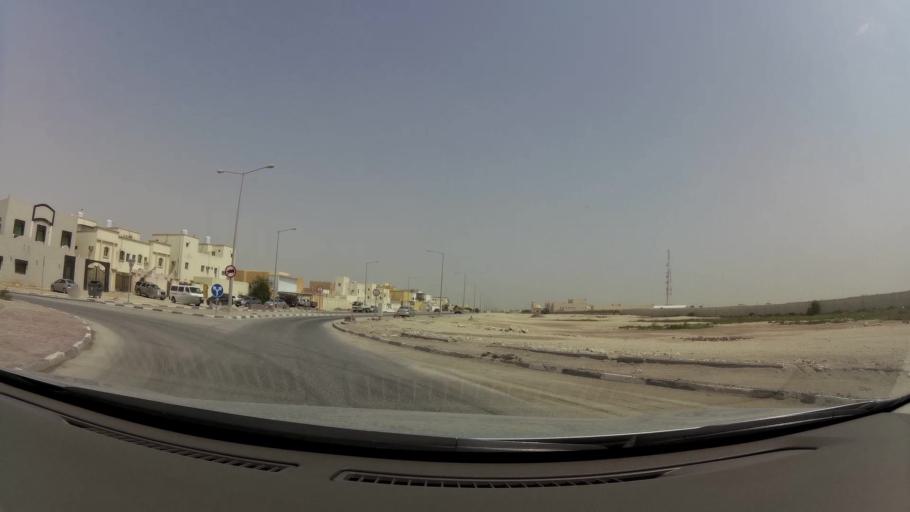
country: QA
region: Baladiyat ar Rayyan
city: Ar Rayyan
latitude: 25.2260
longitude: 51.4122
